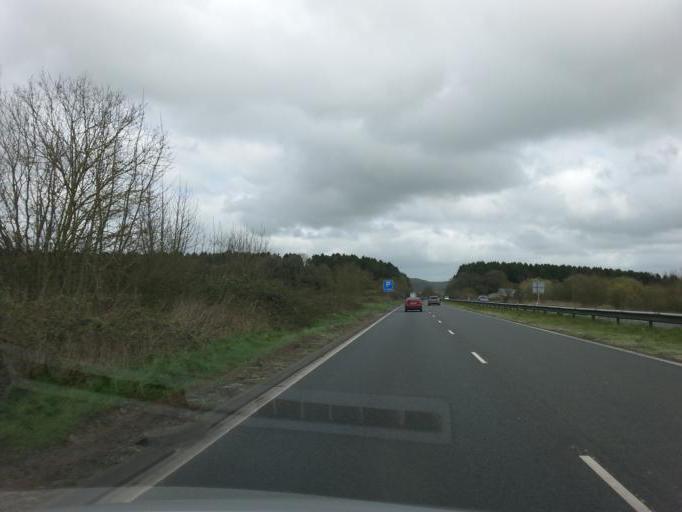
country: GB
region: England
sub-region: Wiltshire
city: Mere
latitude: 51.0909
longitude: -2.2934
